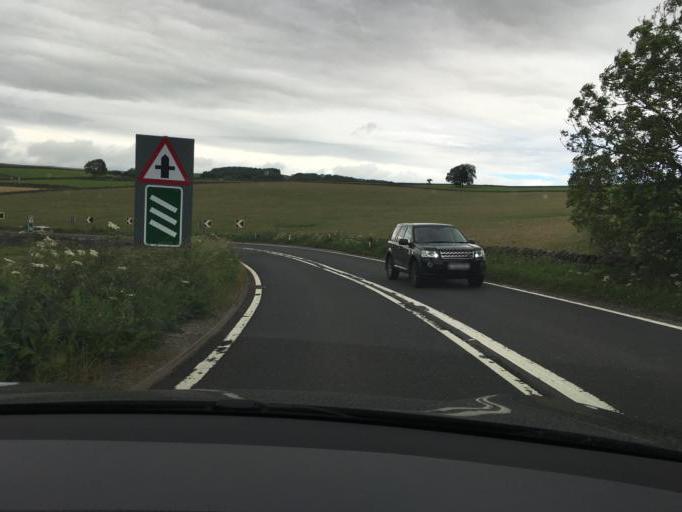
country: GB
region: England
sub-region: Derbyshire
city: Tideswell
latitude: 53.2931
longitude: -1.7836
